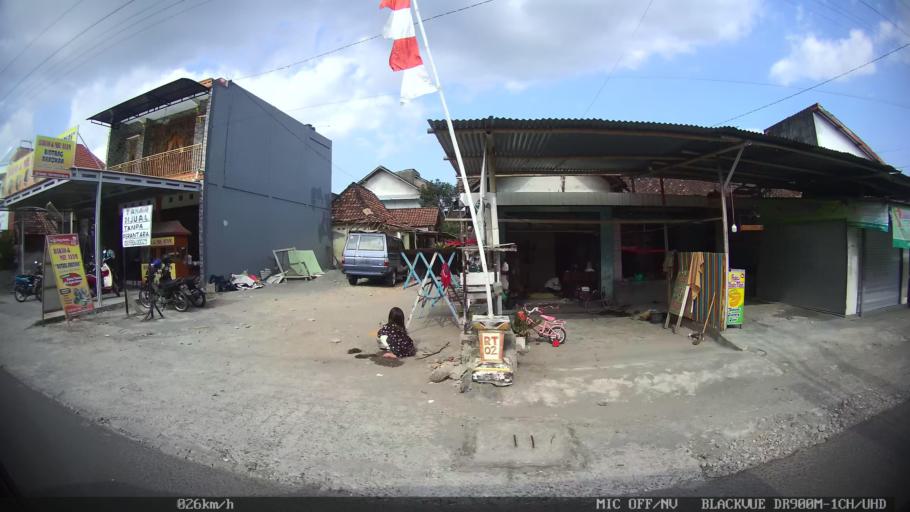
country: ID
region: Daerah Istimewa Yogyakarta
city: Yogyakarta
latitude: -7.7912
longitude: 110.3478
